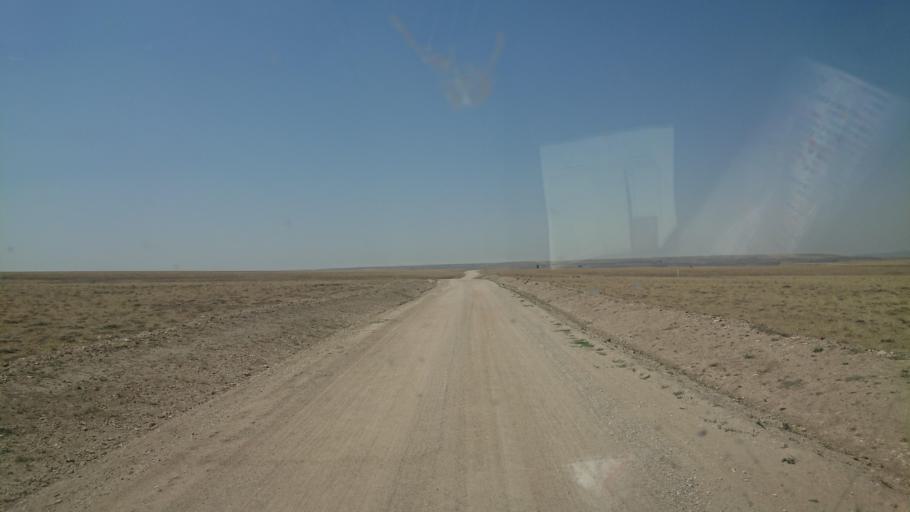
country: TR
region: Aksaray
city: Agacoren
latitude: 38.7422
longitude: 33.8873
